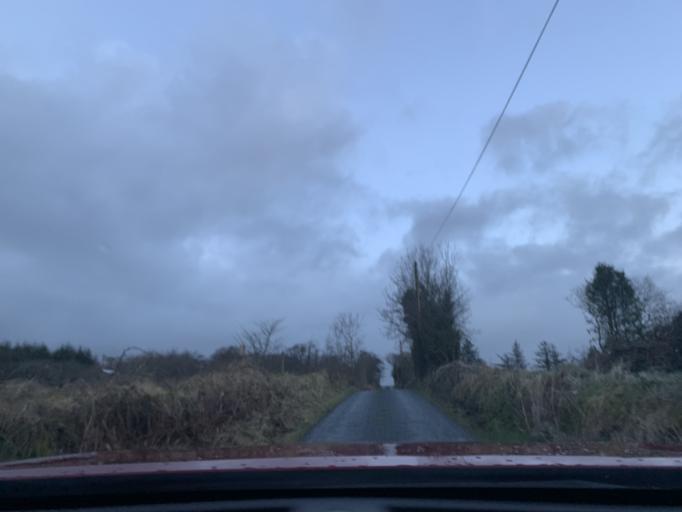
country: IE
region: Connaught
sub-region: Roscommon
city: Ballaghaderreen
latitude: 53.9750
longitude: -8.5600
